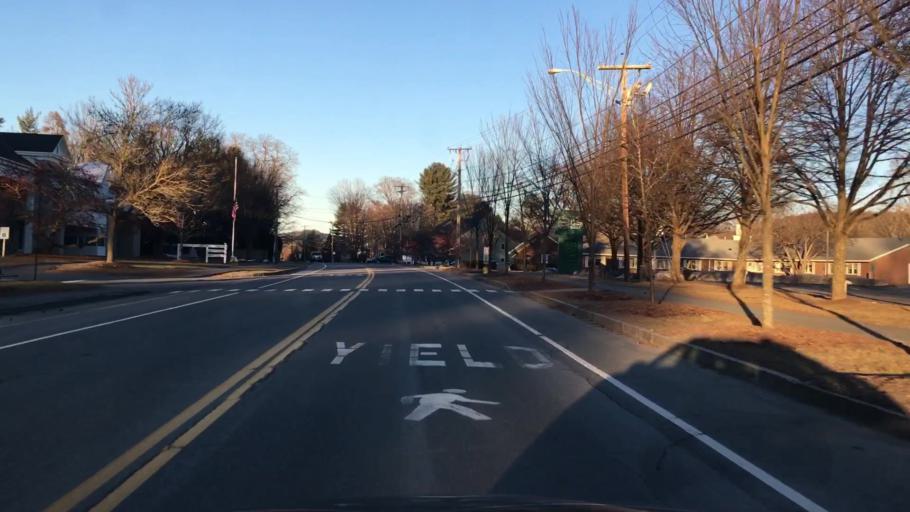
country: US
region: New Hampshire
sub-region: Grafton County
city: Hanover
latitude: 43.7190
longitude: -72.2734
